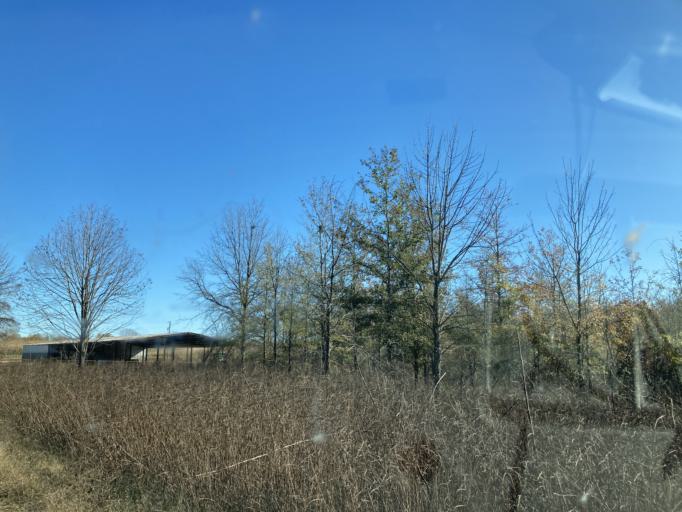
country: US
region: Mississippi
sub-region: Sharkey County
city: Rolling Fork
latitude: 32.7490
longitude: -90.6643
